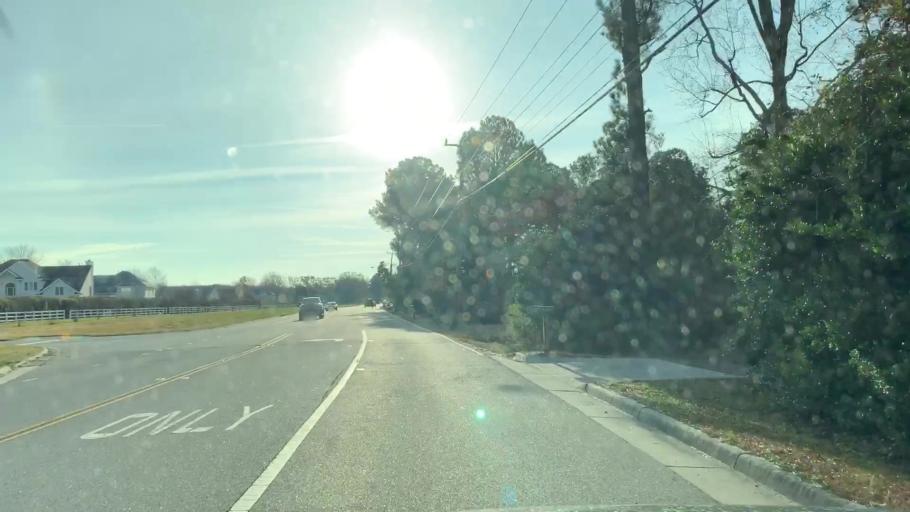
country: US
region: Virginia
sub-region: City of Chesapeake
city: Chesapeake
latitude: 36.7601
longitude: -76.1386
